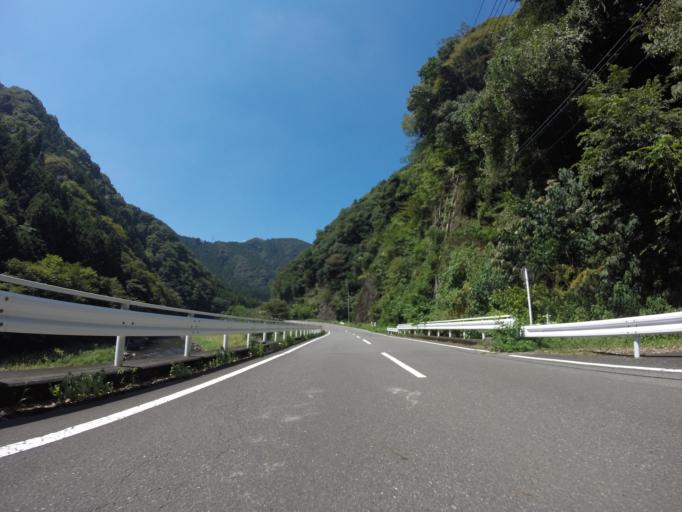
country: JP
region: Shizuoka
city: Shizuoka-shi
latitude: 35.0407
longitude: 138.2568
